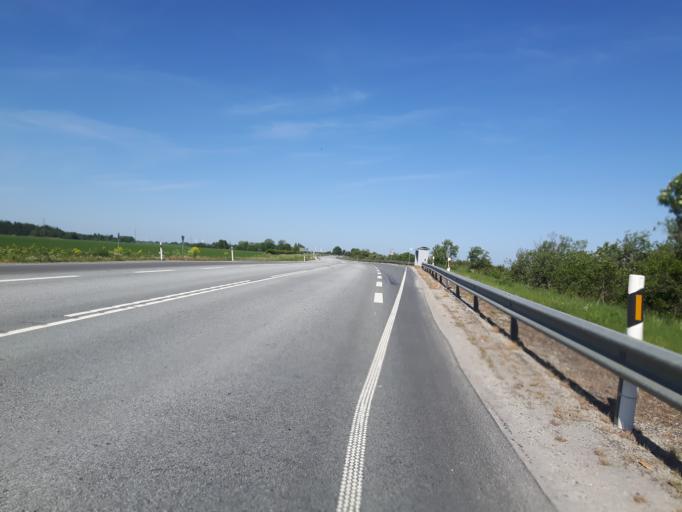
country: EE
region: Ida-Virumaa
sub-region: Aseri vald
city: Aseri
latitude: 59.4331
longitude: 26.9384
